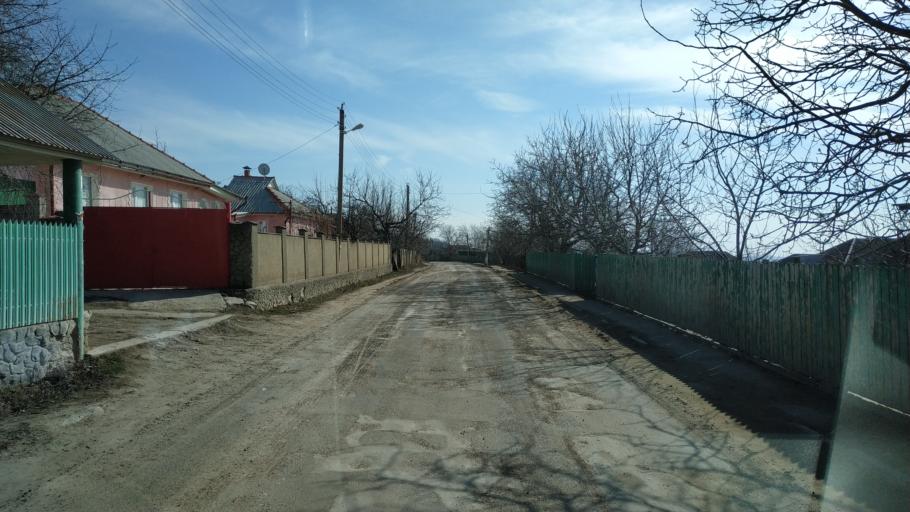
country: MD
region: Nisporeni
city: Nisporeni
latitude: 47.2246
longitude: 28.0377
